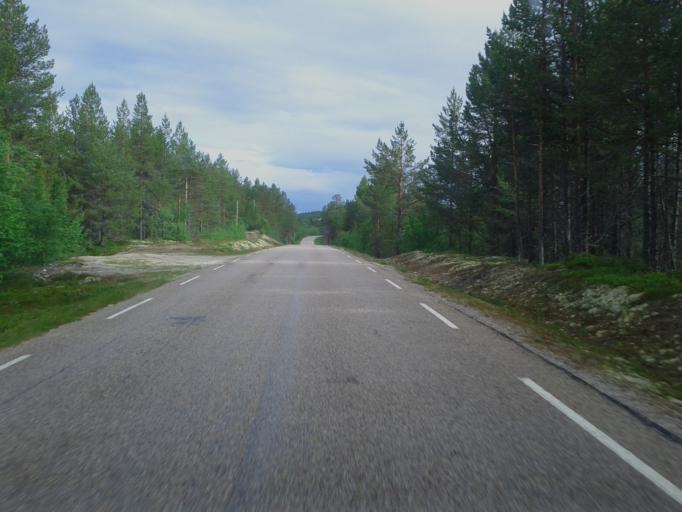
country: NO
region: Hedmark
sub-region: Engerdal
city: Engerdal
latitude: 62.0601
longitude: 11.6811
